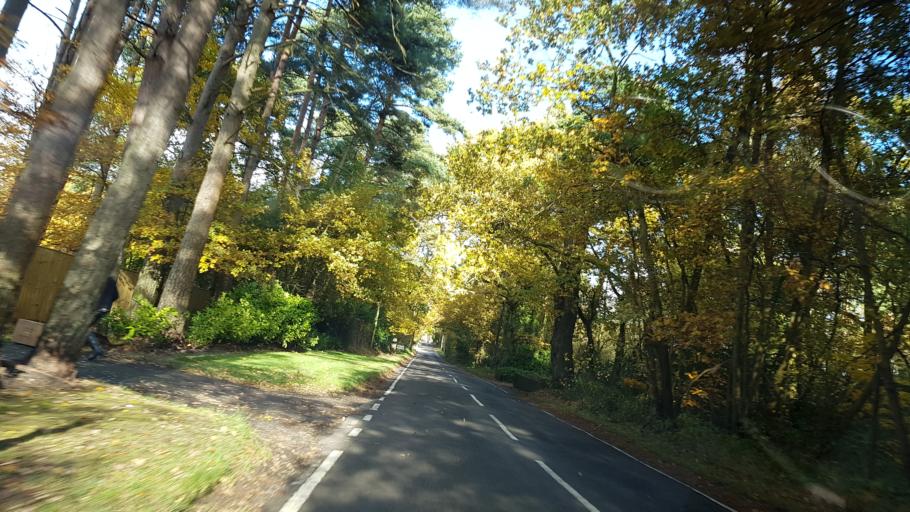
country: GB
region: England
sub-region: Surrey
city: Elstead
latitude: 51.1672
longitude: -0.7153
